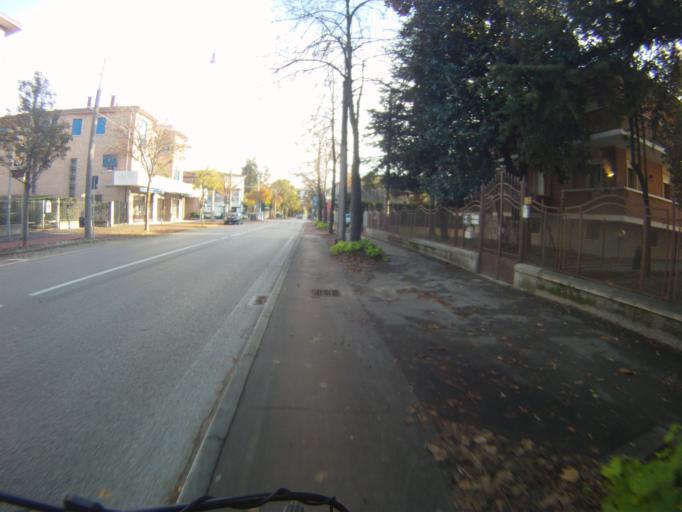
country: IT
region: Veneto
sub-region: Provincia di Padova
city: Padova
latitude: 45.3896
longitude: 11.8940
